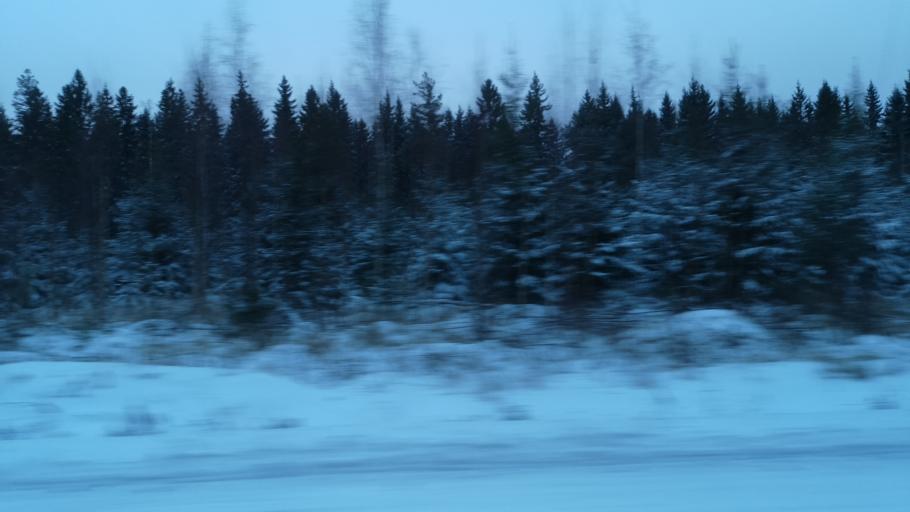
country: FI
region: Southern Savonia
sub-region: Savonlinna
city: Enonkoski
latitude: 62.0784
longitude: 28.7088
